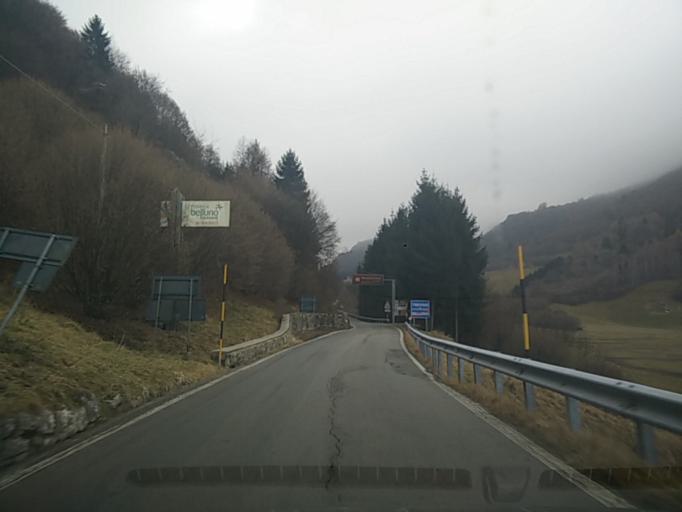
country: IT
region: Veneto
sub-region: Provincia di Treviso
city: Cison di Valmarino
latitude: 46.0143
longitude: 12.1672
